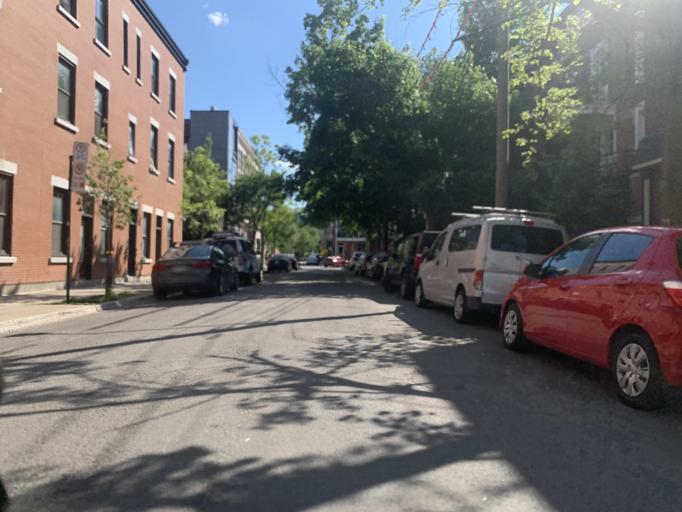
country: CA
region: Quebec
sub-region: Montreal
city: Montreal
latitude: 45.5259
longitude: -73.5778
